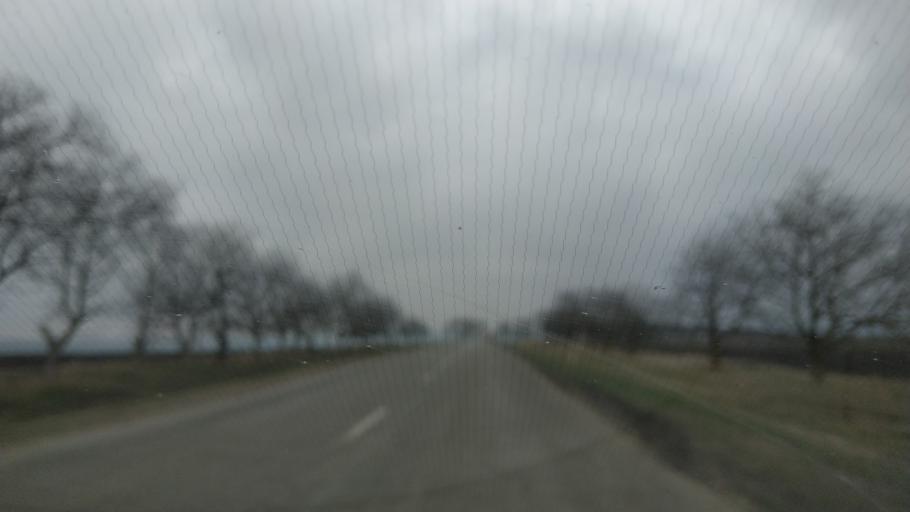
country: MD
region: Gagauzia
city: Comrat
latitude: 46.2625
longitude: 28.7463
